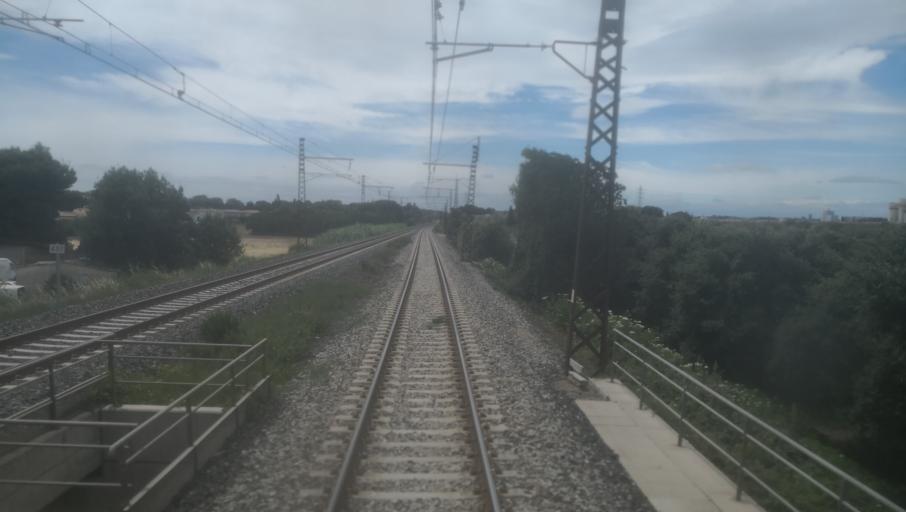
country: FR
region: Languedoc-Roussillon
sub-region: Departement de l'Herault
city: Villeneuve-les-Beziers
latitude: 43.3253
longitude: 3.2805
